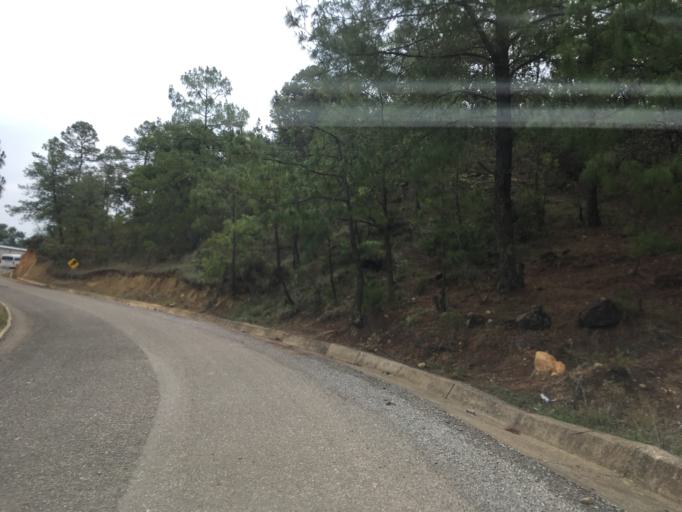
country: MX
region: Oaxaca
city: Santiago Tilantongo
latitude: 17.2214
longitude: -97.2809
